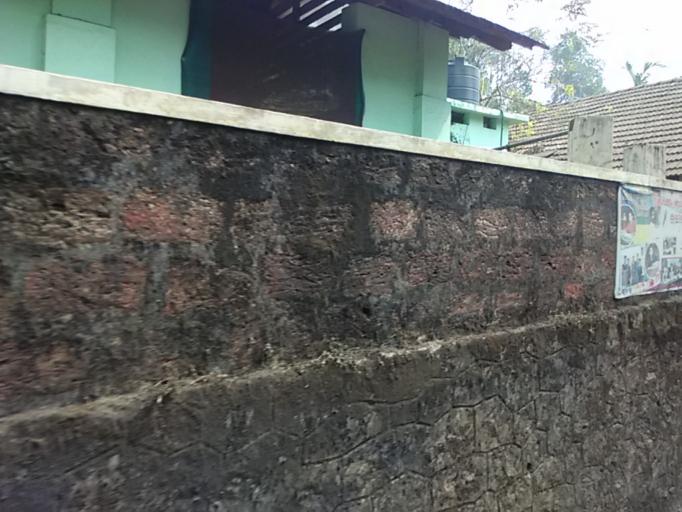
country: IN
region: Kerala
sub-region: Kozhikode
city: Kunnamangalam
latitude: 11.2824
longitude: 75.8509
